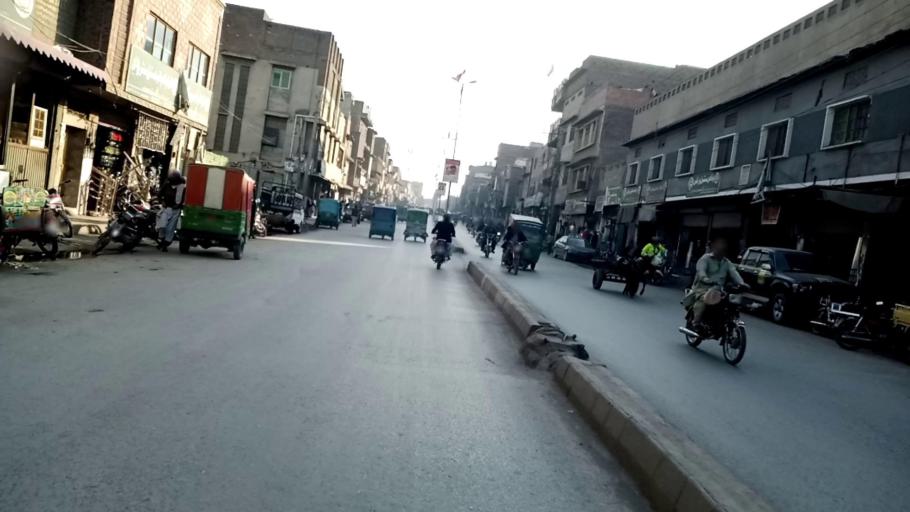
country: PK
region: Khyber Pakhtunkhwa
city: Peshawar
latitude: 34.0095
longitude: 71.5852
